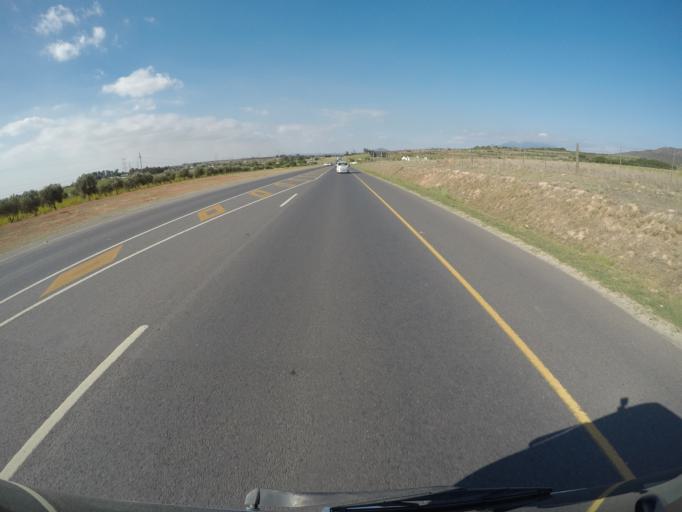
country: ZA
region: Western Cape
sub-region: City of Cape Town
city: Kraaifontein
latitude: -33.8921
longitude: 18.7395
